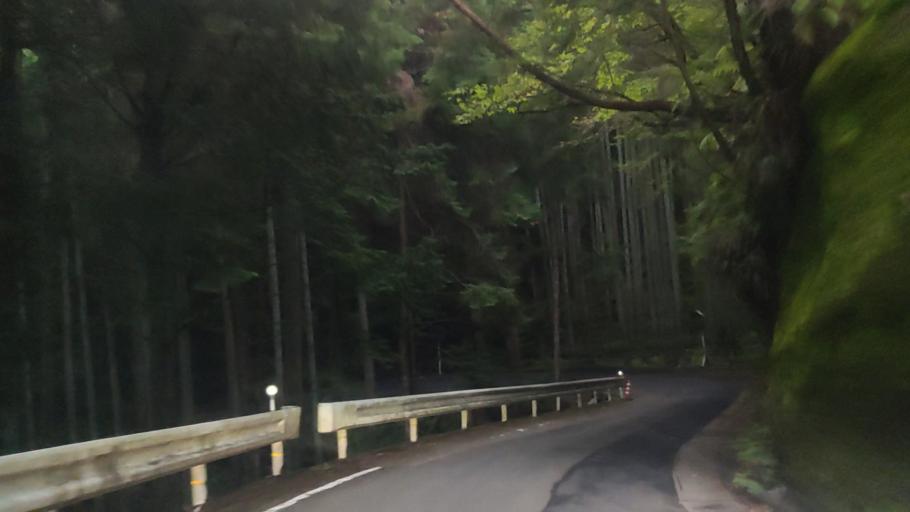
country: JP
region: Wakayama
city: Hashimoto
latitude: 34.3024
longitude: 135.6285
